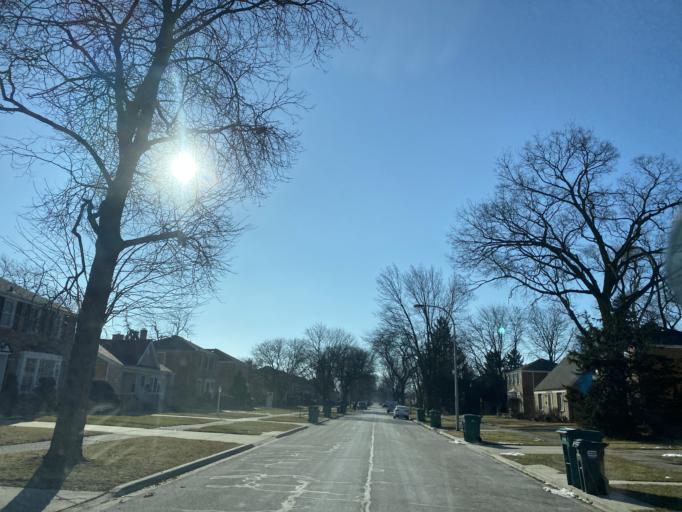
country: US
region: Illinois
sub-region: Cook County
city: Westchester
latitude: 41.8553
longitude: -87.8698
